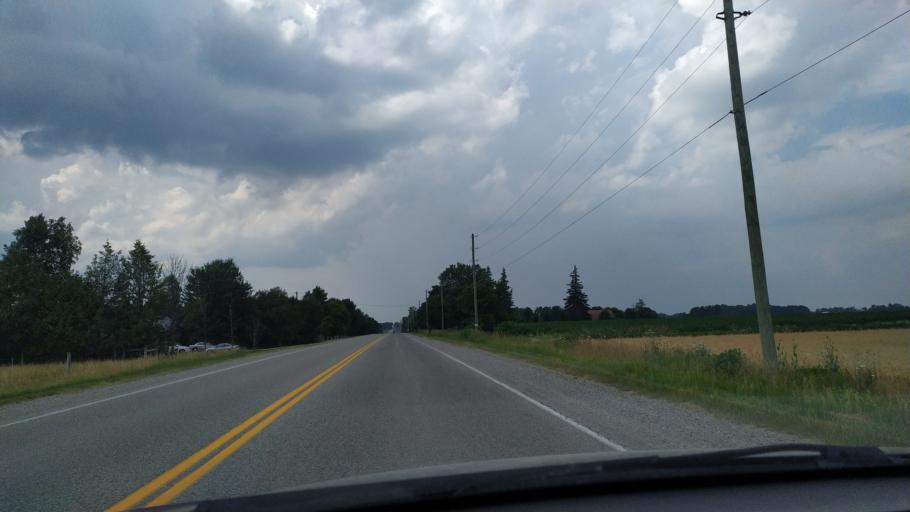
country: CA
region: Ontario
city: London
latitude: 43.1365
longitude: -81.1746
